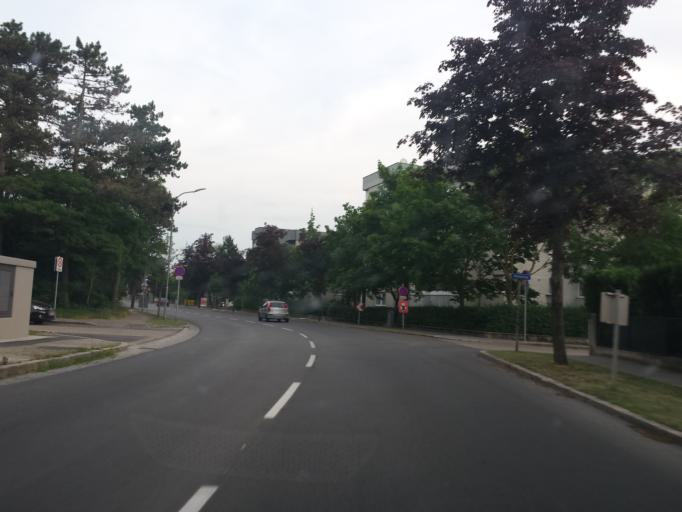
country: AT
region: Lower Austria
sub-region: Politischer Bezirk Ganserndorf
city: Deutsch-Wagram
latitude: 48.3083
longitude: 16.5698
